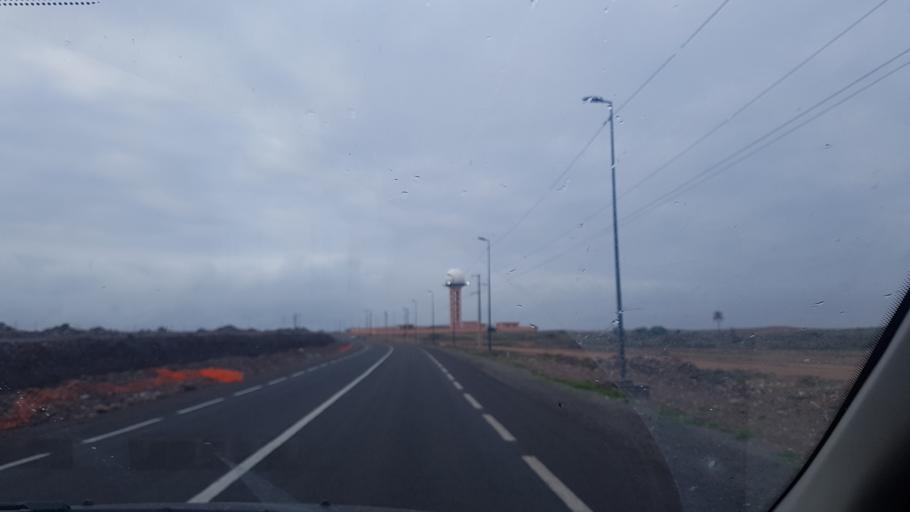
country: MA
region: Marrakech-Tensift-Al Haouz
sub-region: Marrakech
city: Marrakesh
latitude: 31.5589
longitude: -8.0643
